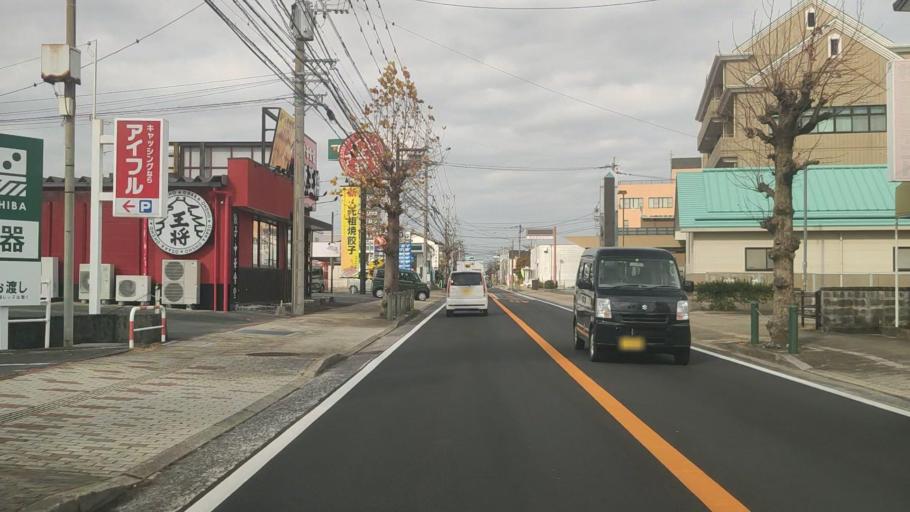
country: JP
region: Nagasaki
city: Shimabara
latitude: 32.7971
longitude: 130.3669
